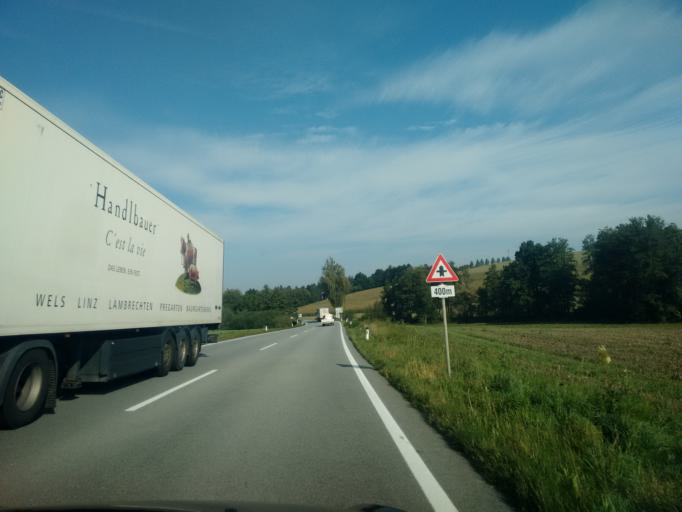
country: AT
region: Upper Austria
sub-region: Politischer Bezirk Ried im Innkreis
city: Ried im Innkreis
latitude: 48.2990
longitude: 13.6410
